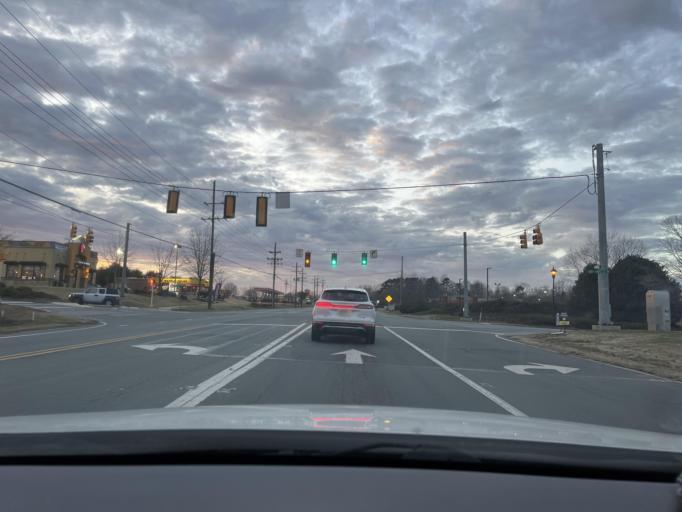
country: US
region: North Carolina
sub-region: Guilford County
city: McLeansville
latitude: 36.0627
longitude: -79.6054
